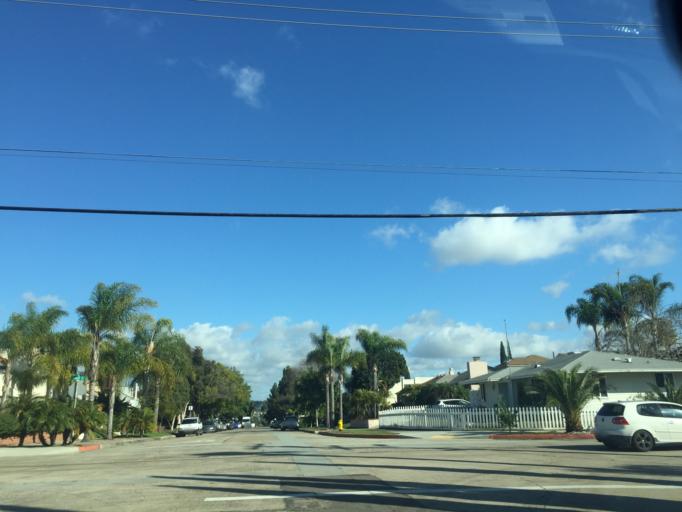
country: US
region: California
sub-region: San Diego County
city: La Jolla
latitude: 32.7963
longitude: -117.2381
